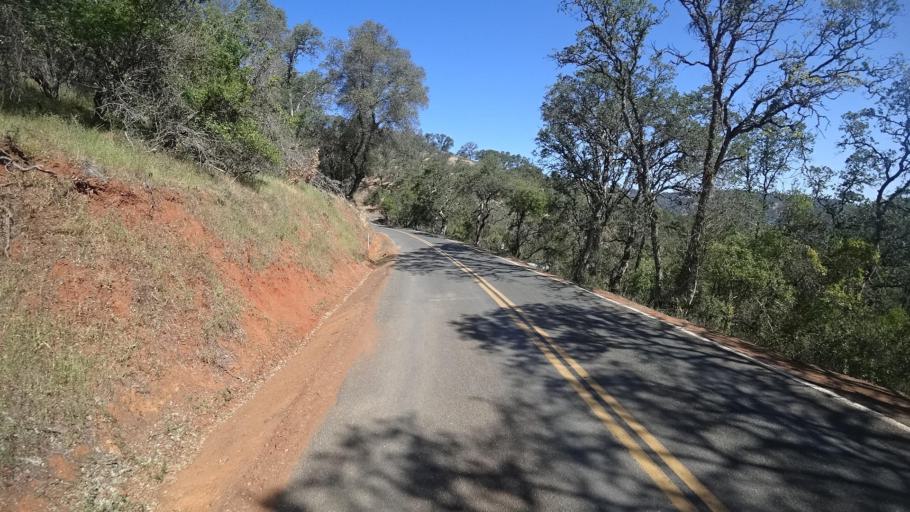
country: US
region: California
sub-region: Lake County
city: Clearlake Oaks
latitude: 38.9994
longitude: -122.7011
